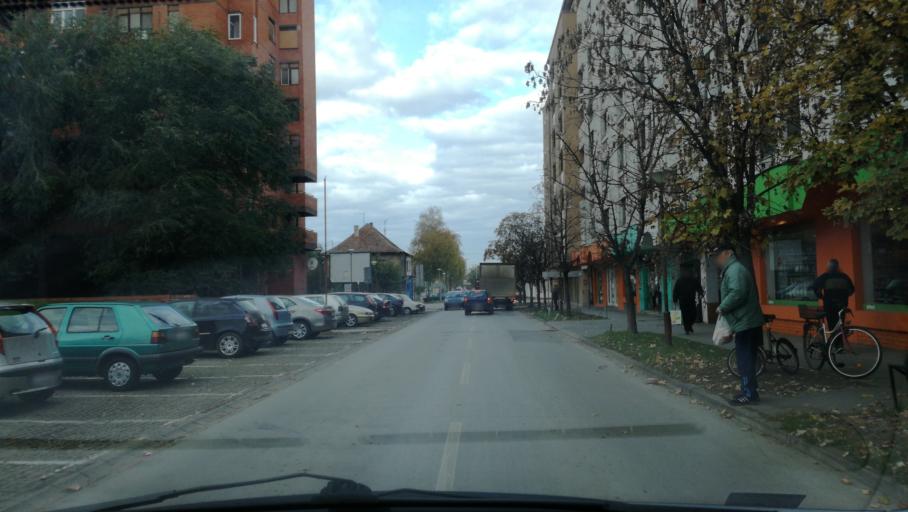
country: RS
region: Autonomna Pokrajina Vojvodina
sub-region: Severnobanatski Okrug
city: Kikinda
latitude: 45.8286
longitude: 20.4625
